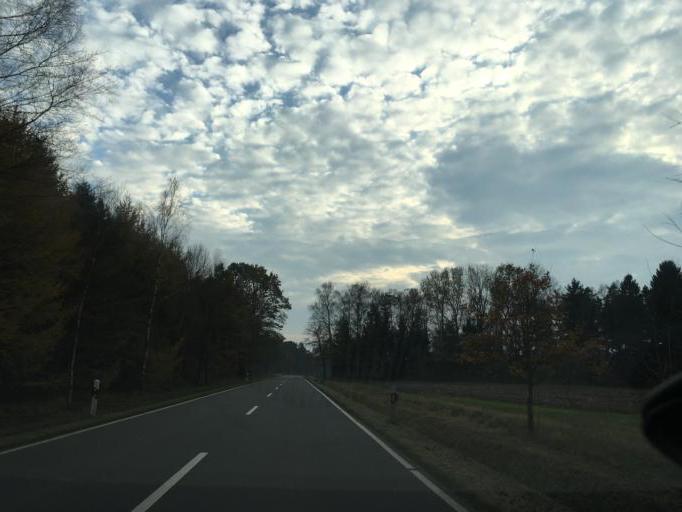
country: DE
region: Lower Saxony
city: Bispingen
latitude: 53.0107
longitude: 9.9978
